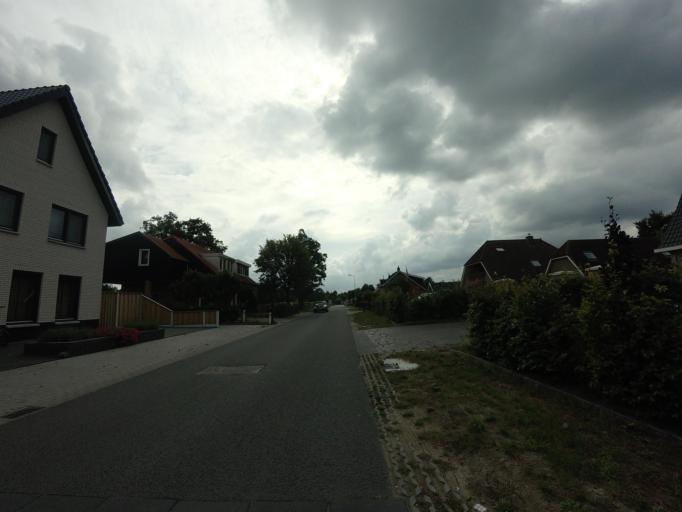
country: DE
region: North Rhine-Westphalia
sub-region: Regierungsbezirk Munster
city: Gronau
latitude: 52.2062
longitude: 6.9620
